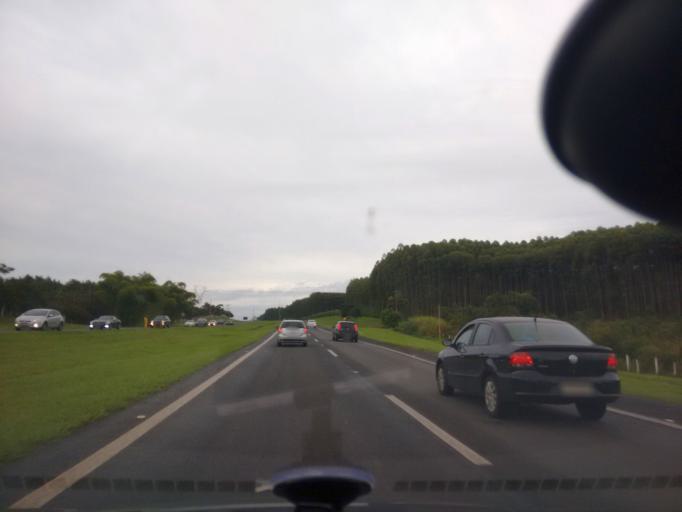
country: BR
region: Sao Paulo
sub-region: Itirapina
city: Itirapina
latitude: -22.1467
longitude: -47.7972
